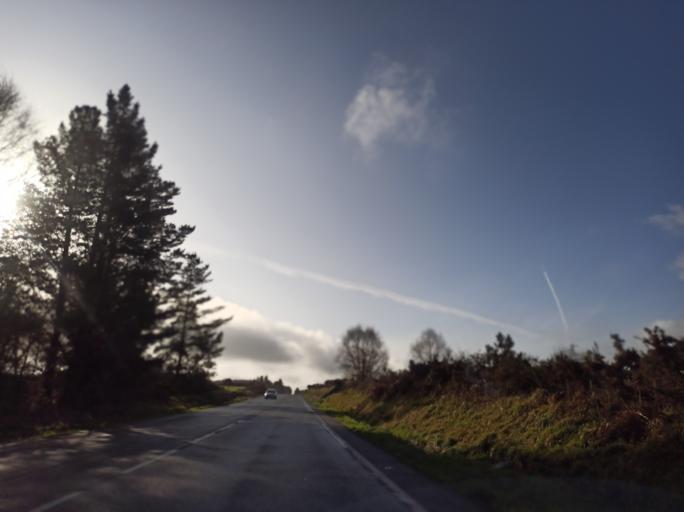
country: ES
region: Galicia
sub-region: Provincia da Coruna
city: Curtis
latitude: 43.1177
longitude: -8.0279
